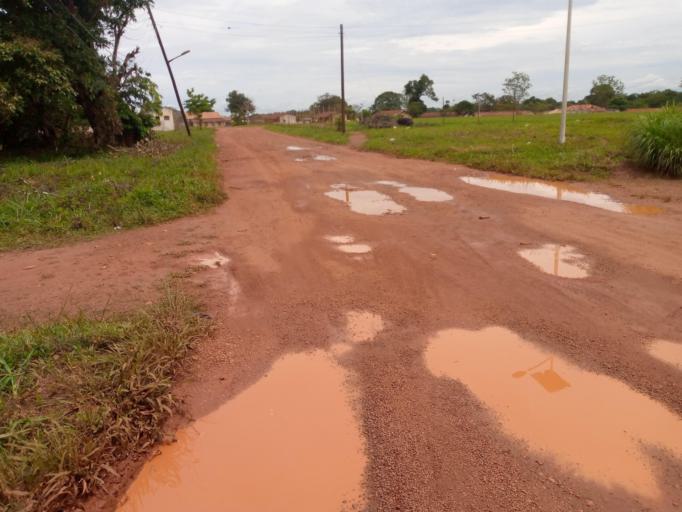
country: SL
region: Southern Province
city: Largo
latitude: 8.1165
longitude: -12.0691
